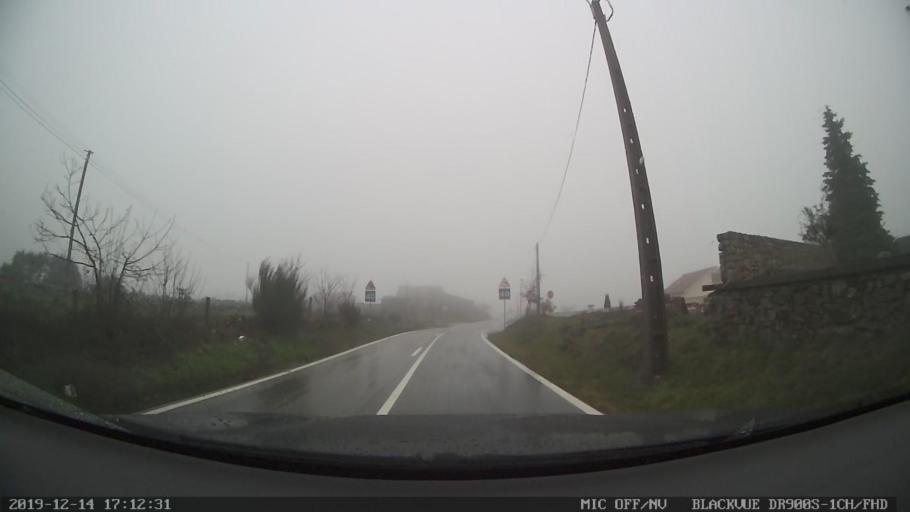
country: PT
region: Vila Real
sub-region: Vila Pouca de Aguiar
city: Vila Pouca de Aguiar
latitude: 41.4943
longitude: -7.6212
